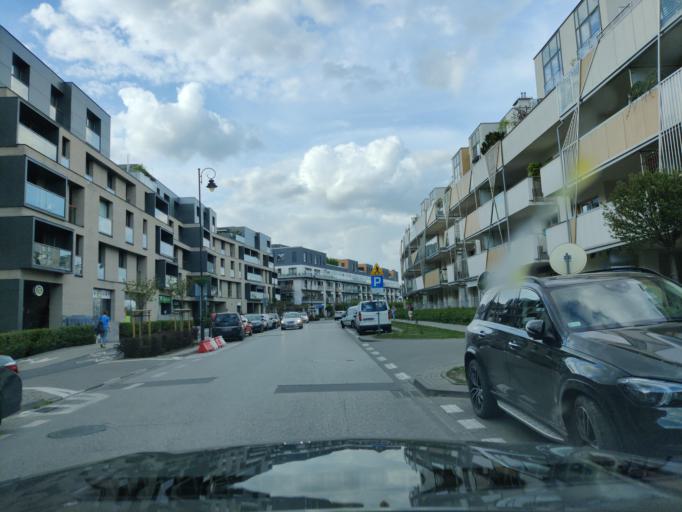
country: PL
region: Masovian Voivodeship
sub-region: Warszawa
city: Wilanow
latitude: 52.1655
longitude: 21.0746
